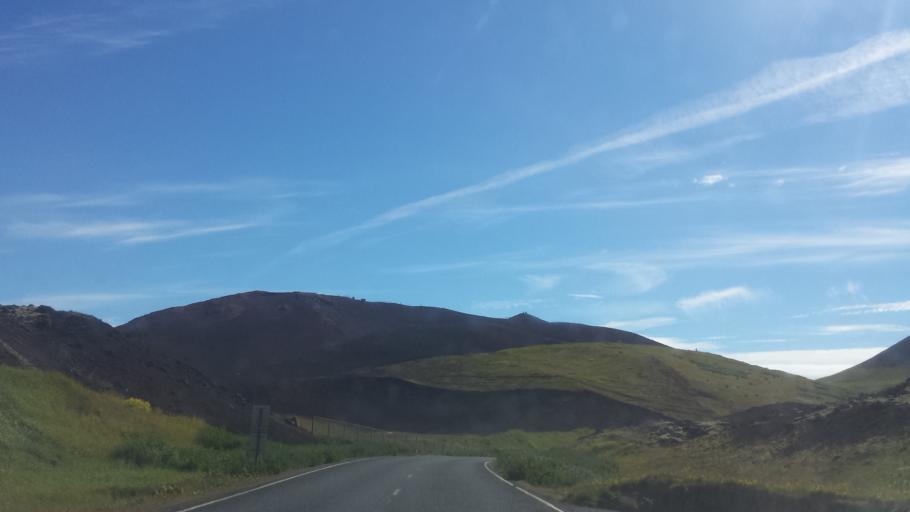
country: IS
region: South
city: Vestmannaeyjar
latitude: 63.4390
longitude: -20.2568
